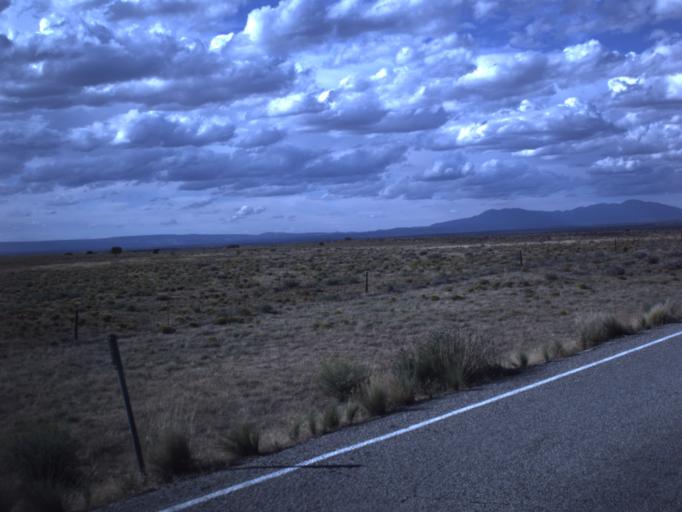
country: US
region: Utah
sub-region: San Juan County
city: Blanding
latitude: 37.3521
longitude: -109.3470
